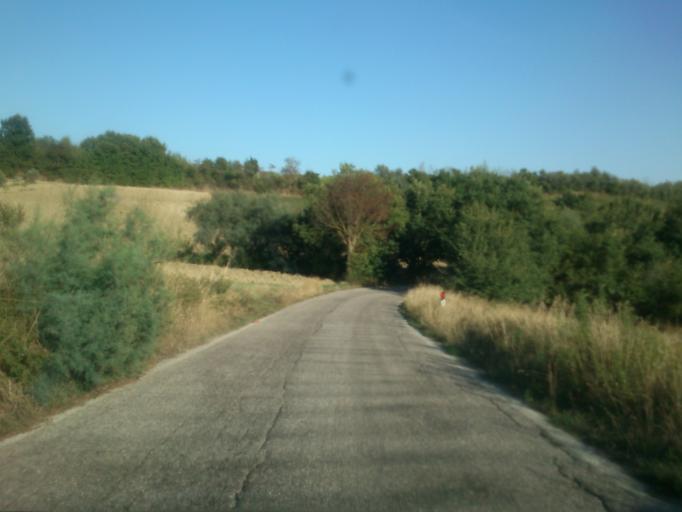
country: IT
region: The Marches
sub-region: Provincia di Pesaro e Urbino
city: Cartoceto
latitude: 43.7848
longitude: 12.9064
